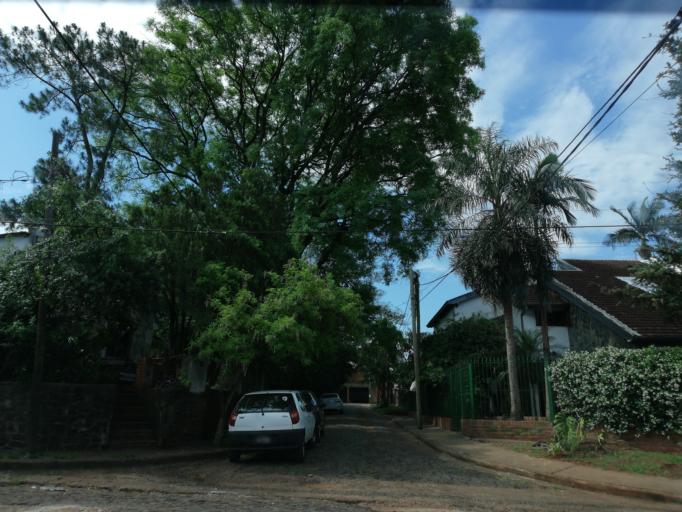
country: AR
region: Misiones
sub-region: Departamento de Capital
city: Posadas
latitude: -27.3798
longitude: -55.9043
